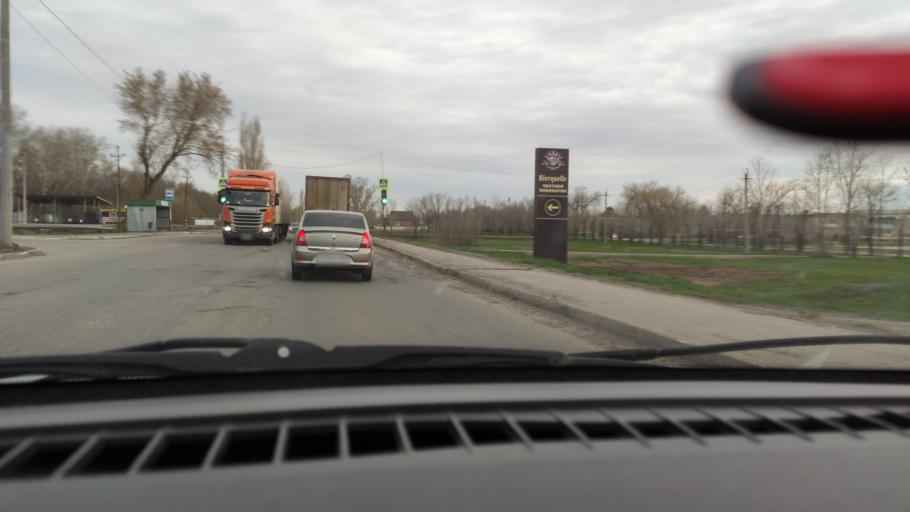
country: RU
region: Orenburg
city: Tatarskaya Kargala
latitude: 51.8663
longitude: 55.1404
